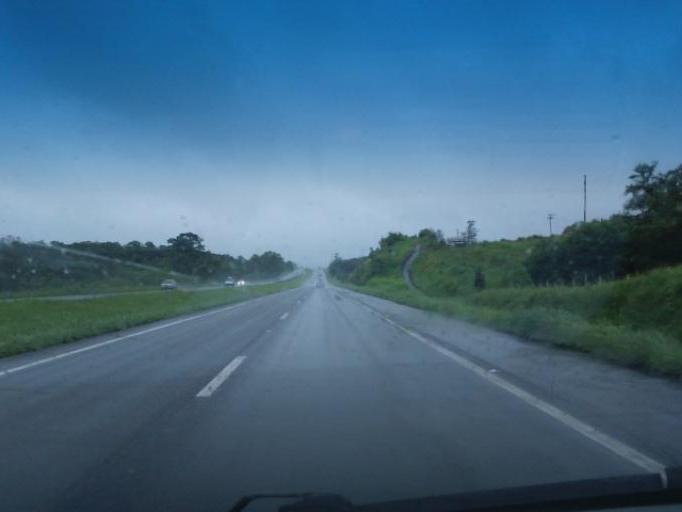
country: BR
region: Sao Paulo
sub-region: Jacupiranga
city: Jacupiranga
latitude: -24.6538
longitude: -47.9578
